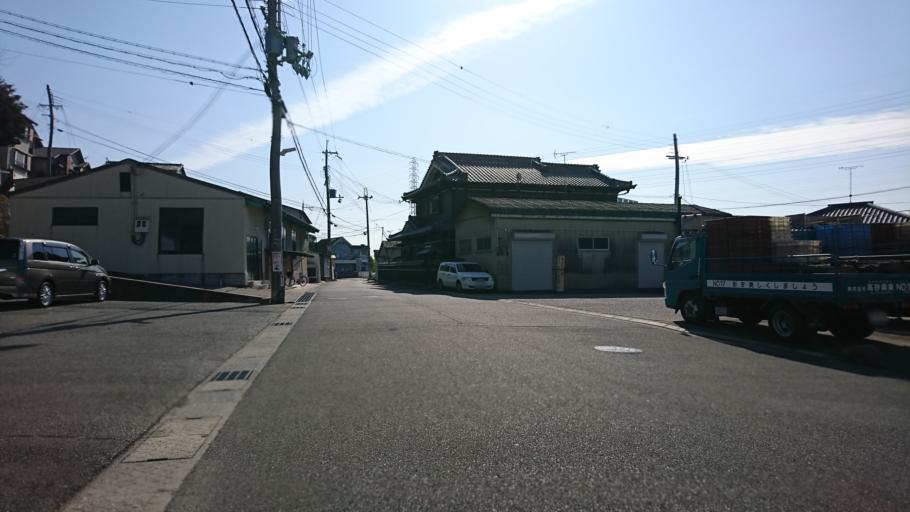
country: JP
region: Hyogo
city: Kakogawacho-honmachi
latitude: 34.7760
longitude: 134.7950
